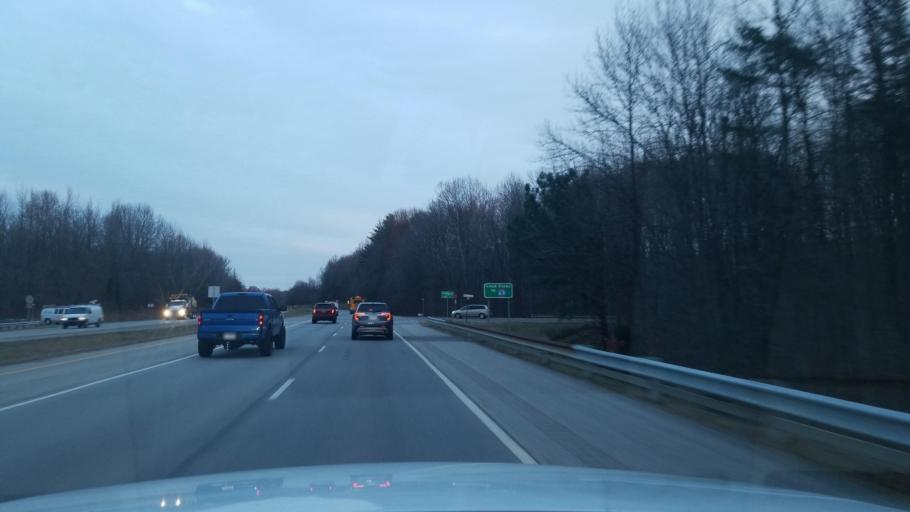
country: US
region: Indiana
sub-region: Vanderburgh County
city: Evansville
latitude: 37.9508
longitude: -87.7001
